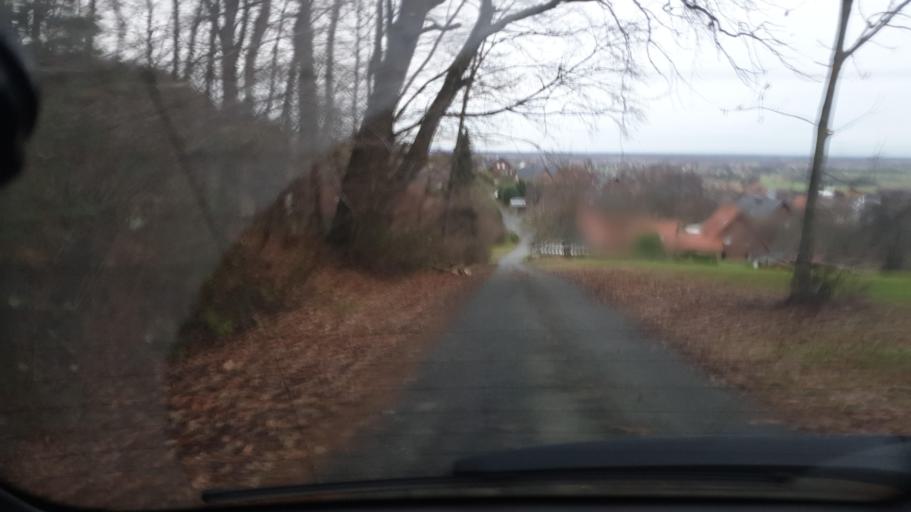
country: DE
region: North Rhine-Westphalia
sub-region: Regierungsbezirk Detmold
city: Hille
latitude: 52.2808
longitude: 8.7525
